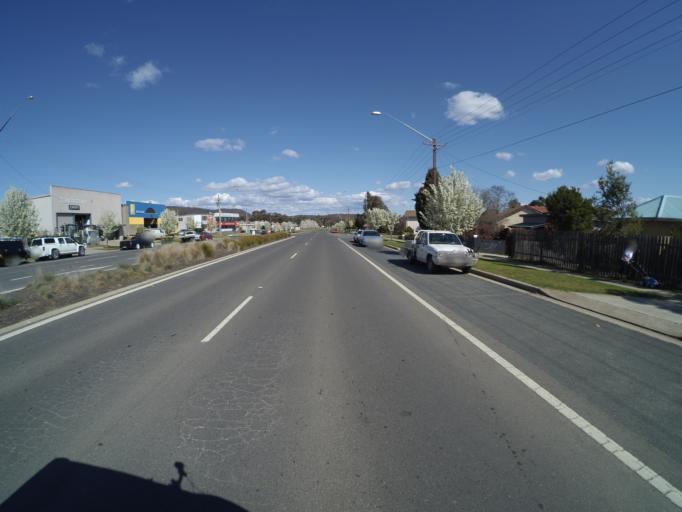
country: AU
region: New South Wales
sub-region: Queanbeyan
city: Queanbeyan
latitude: -35.3421
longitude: 149.2444
